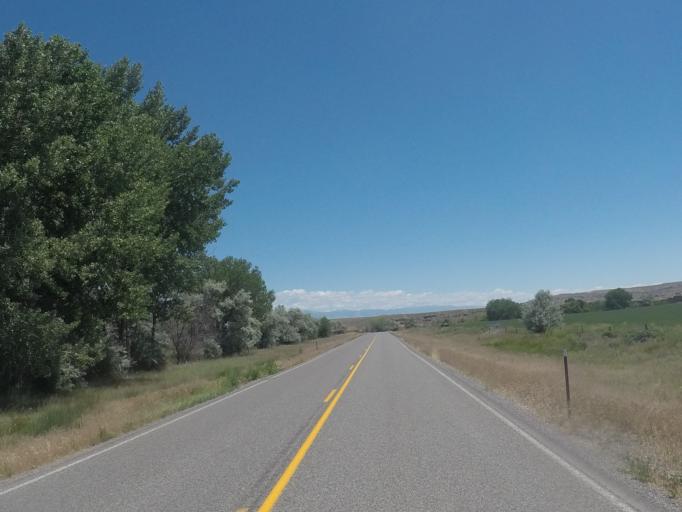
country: US
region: Wyoming
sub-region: Big Horn County
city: Lovell
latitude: 44.7673
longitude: -108.5267
